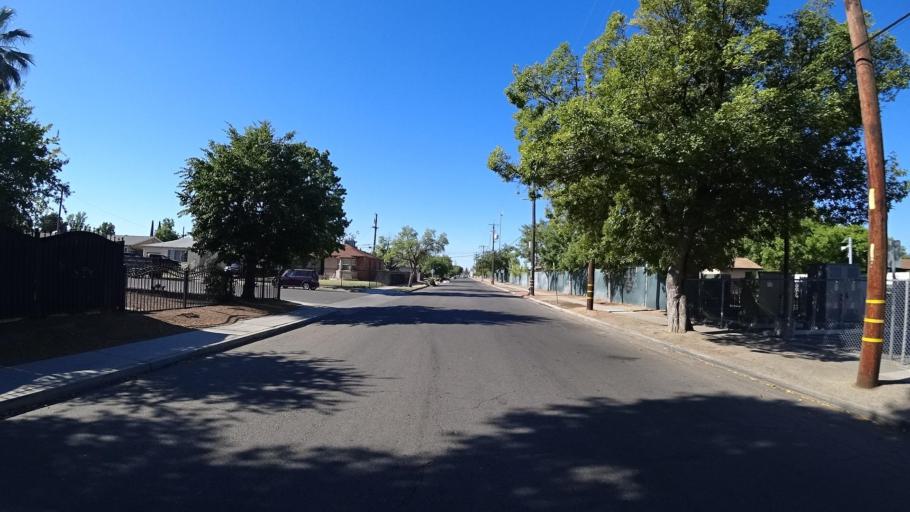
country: US
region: California
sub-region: Fresno County
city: Fresno
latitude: 36.7688
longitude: -119.7860
